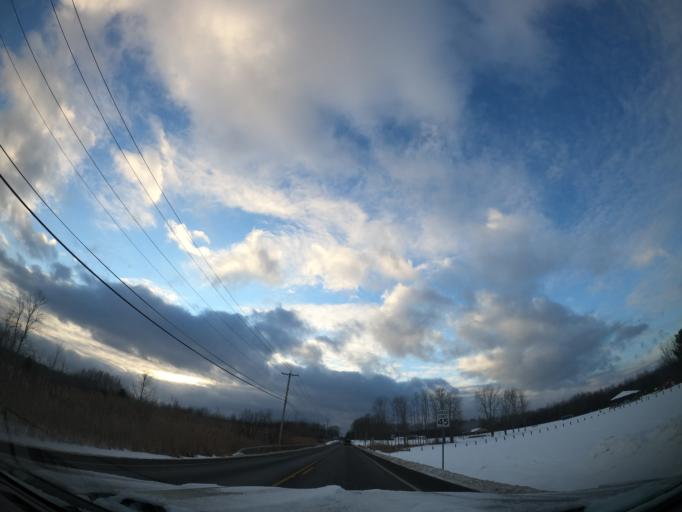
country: US
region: New York
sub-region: Onondaga County
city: Brewerton
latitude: 43.2169
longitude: -76.1380
